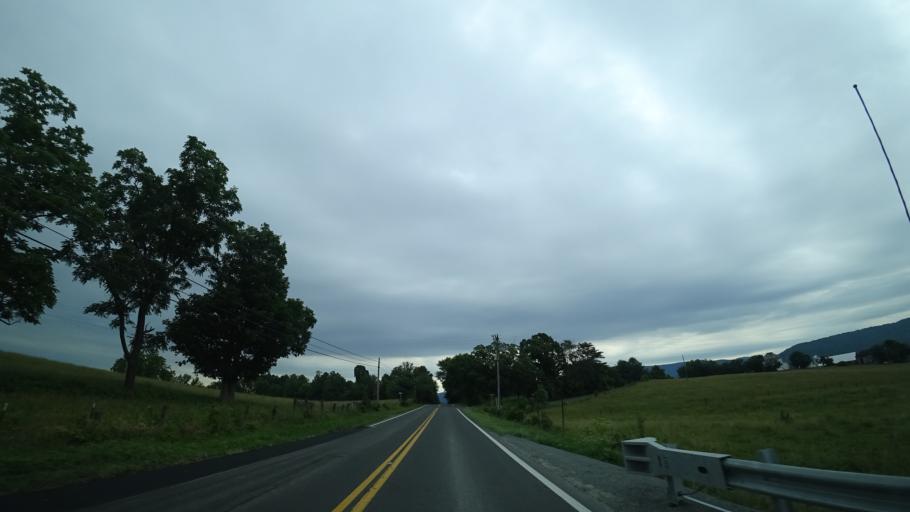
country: US
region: Virginia
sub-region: Warren County
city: Front Royal
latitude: 38.8502
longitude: -78.2869
